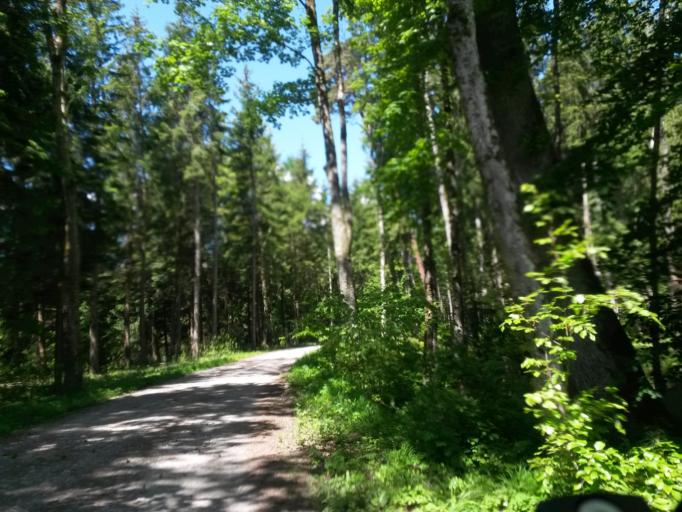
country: DE
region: Baden-Wuerttemberg
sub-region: Tuebingen Region
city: Aulendorf
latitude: 47.9484
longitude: 9.6836
